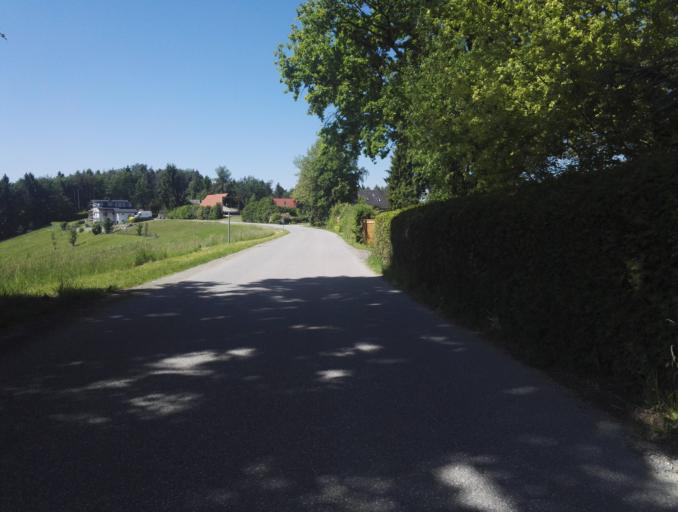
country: AT
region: Styria
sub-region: Politischer Bezirk Graz-Umgebung
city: Edelsgrub
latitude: 47.0537
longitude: 15.5762
